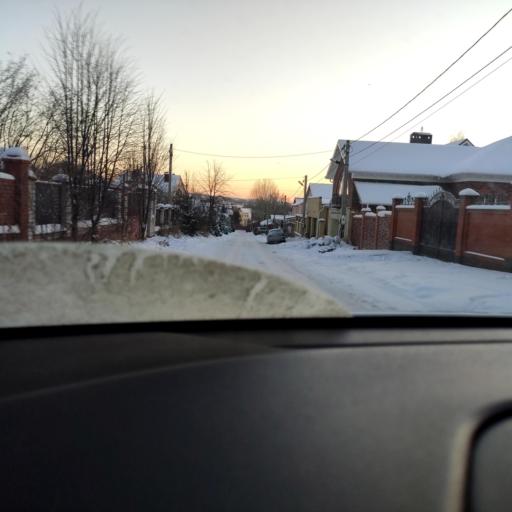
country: RU
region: Tatarstan
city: Stolbishchi
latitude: 55.7481
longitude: 49.2497
